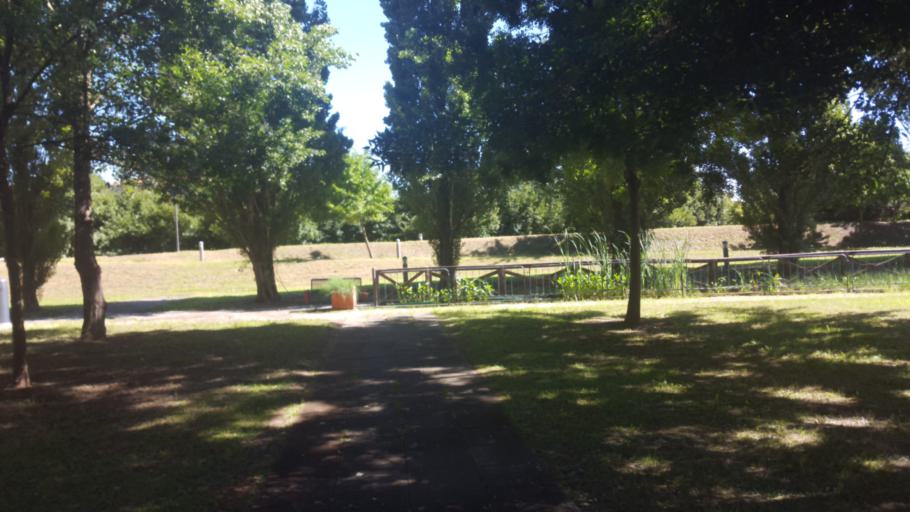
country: IT
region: Veneto
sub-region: Provincia di Venezia
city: San Dona di Piave
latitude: 45.6374
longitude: 12.5704
